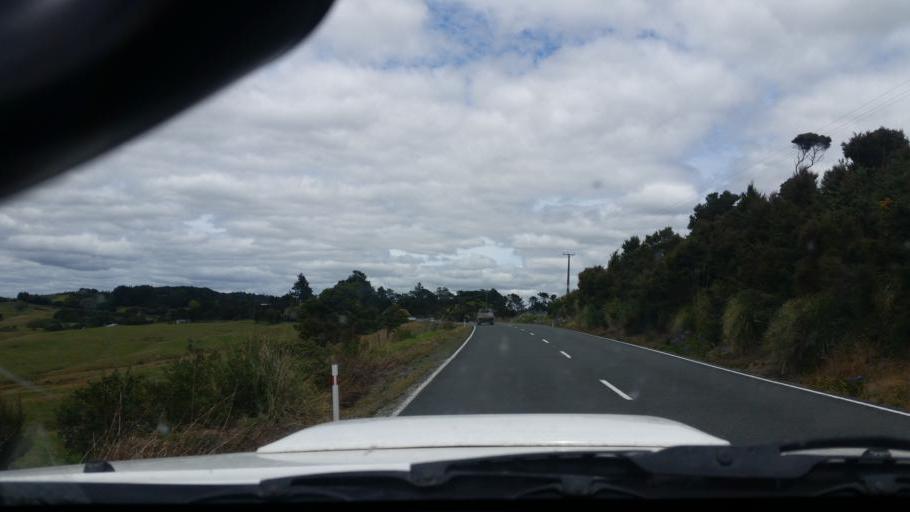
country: NZ
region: Auckland
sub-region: Auckland
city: Wellsford
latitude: -36.1448
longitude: 174.5838
